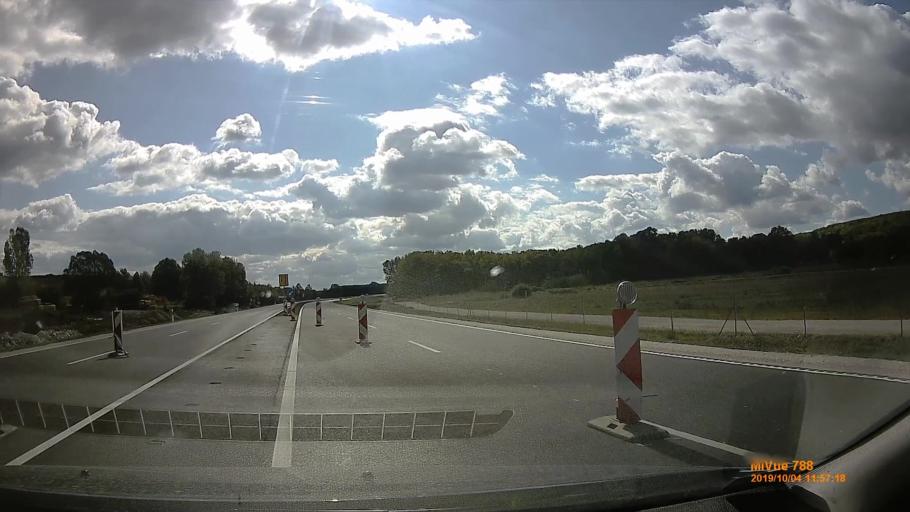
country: HU
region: Somogy
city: Karad
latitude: 46.6620
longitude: 17.7847
